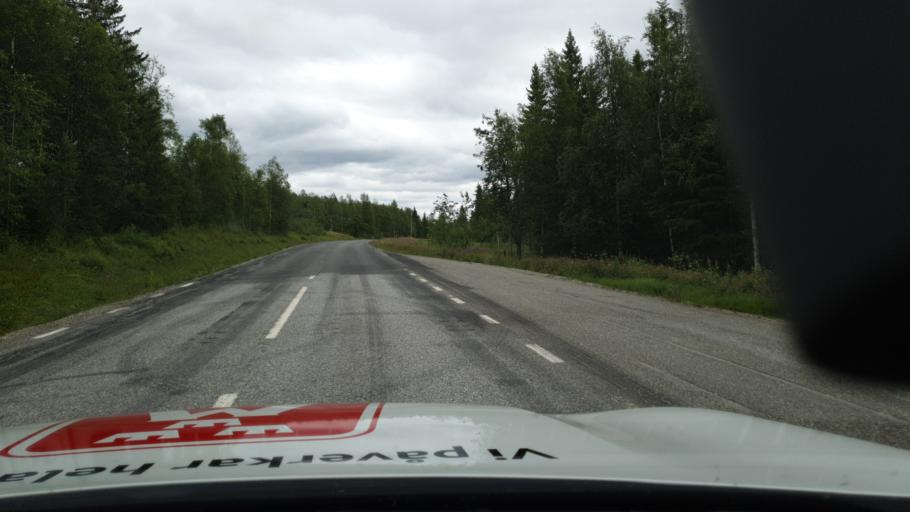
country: SE
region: Vaesterbotten
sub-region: Lycksele Kommun
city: Soderfors
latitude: 64.6458
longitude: 17.8568
